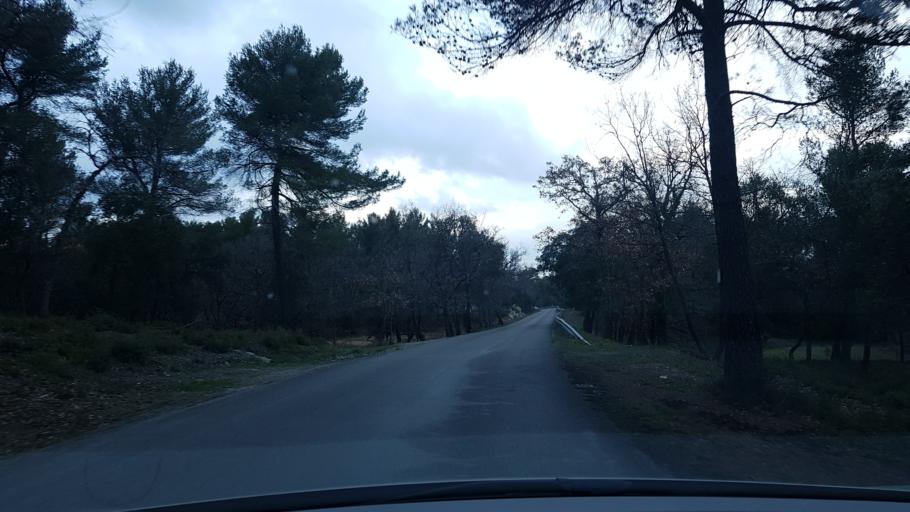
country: FR
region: Provence-Alpes-Cote d'Azur
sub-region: Departement des Bouches-du-Rhone
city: Mimet
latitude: 43.4275
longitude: 5.5092
